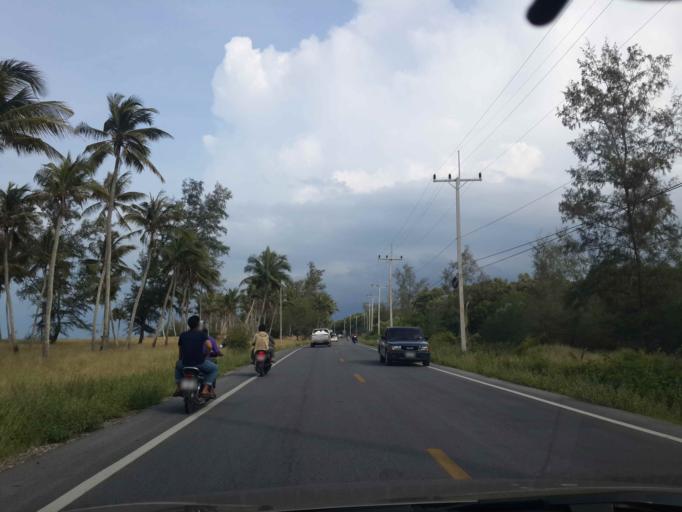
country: TH
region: Pattani
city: Yaring
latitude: 6.9075
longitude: 101.3493
